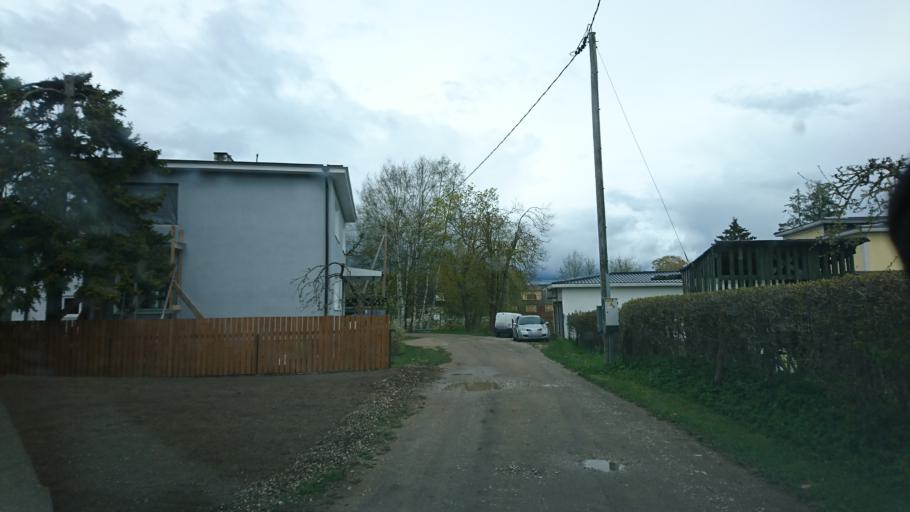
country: EE
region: Laeaene-Virumaa
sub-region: Rakvere linn
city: Rakvere
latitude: 59.3371
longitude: 26.3638
